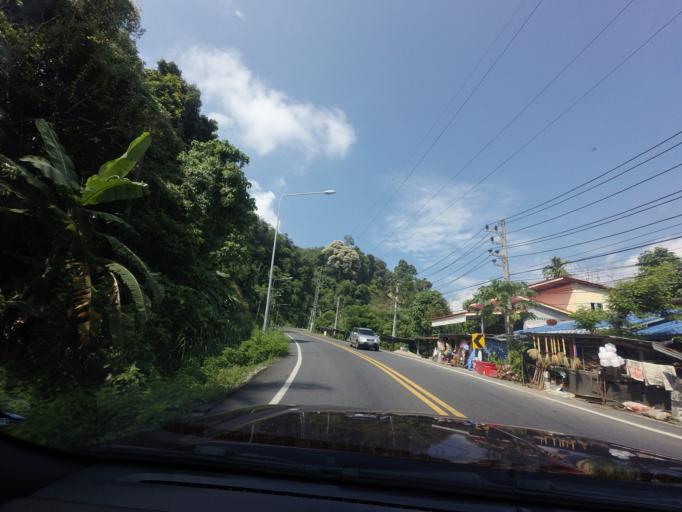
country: TH
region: Yala
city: Betong
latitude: 5.9102
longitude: 101.1523
